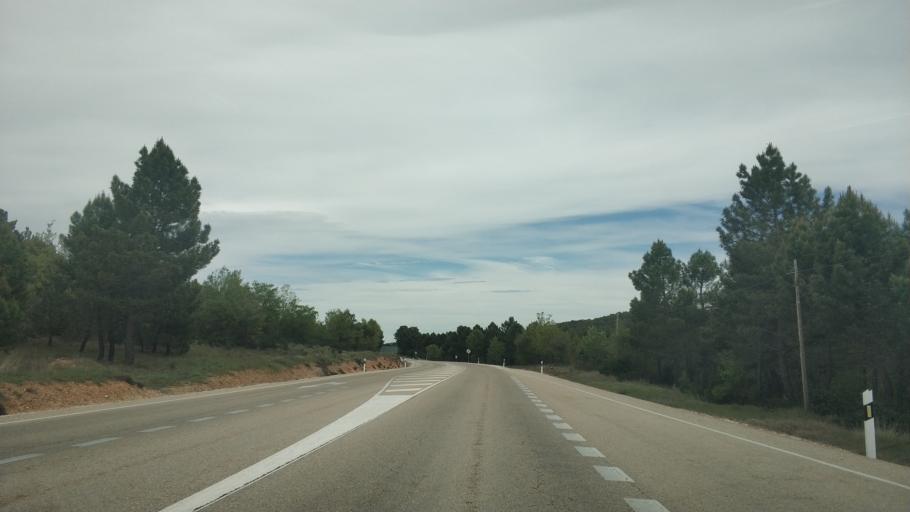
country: ES
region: Castille and Leon
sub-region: Provincia de Soria
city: Bayubas de Abajo
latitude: 41.5112
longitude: -2.9223
